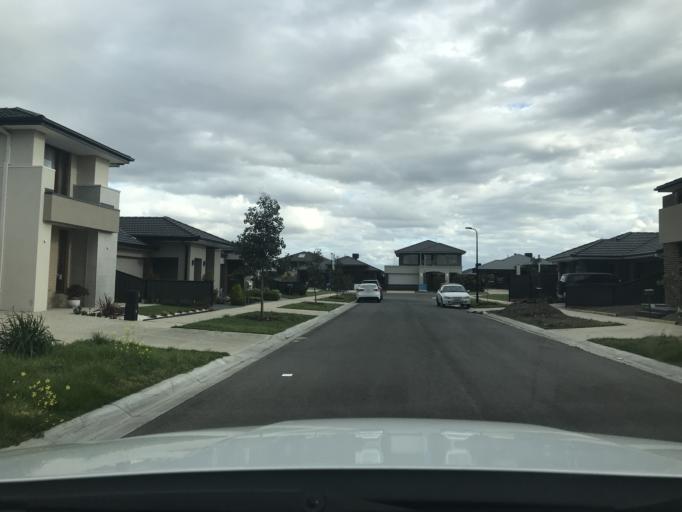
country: AU
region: Victoria
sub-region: Hume
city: Roxburgh Park
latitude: -37.5897
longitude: 144.8913
